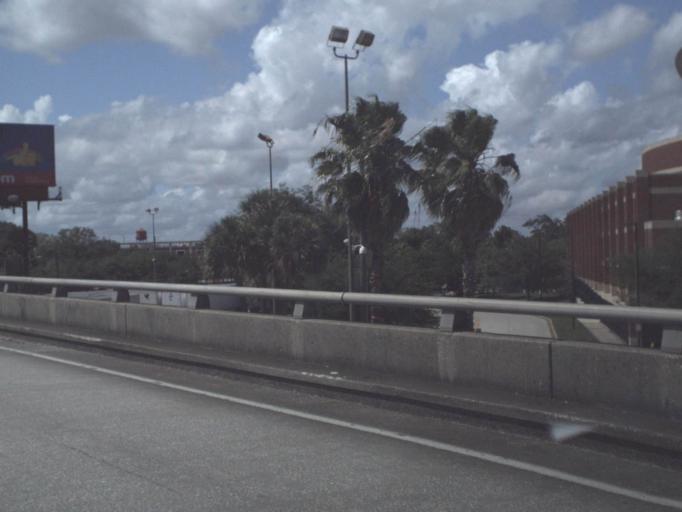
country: US
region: Florida
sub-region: Duval County
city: Jacksonville
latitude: 30.3246
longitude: -81.6463
